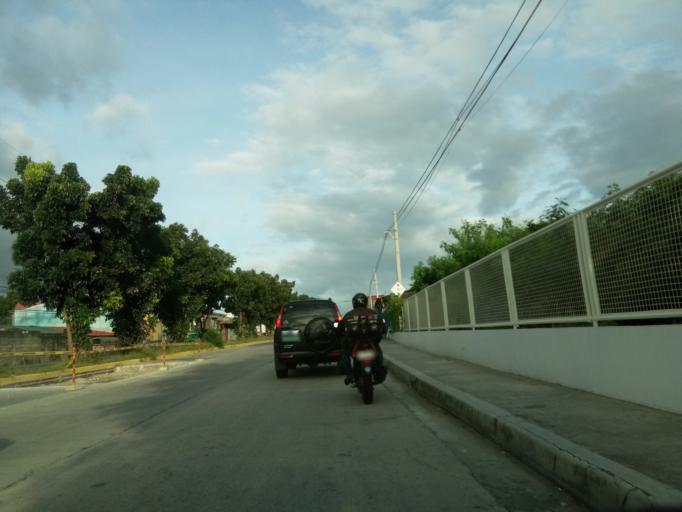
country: PH
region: Calabarzon
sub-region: Province of Cavite
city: Imus
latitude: 14.3882
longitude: 120.9651
